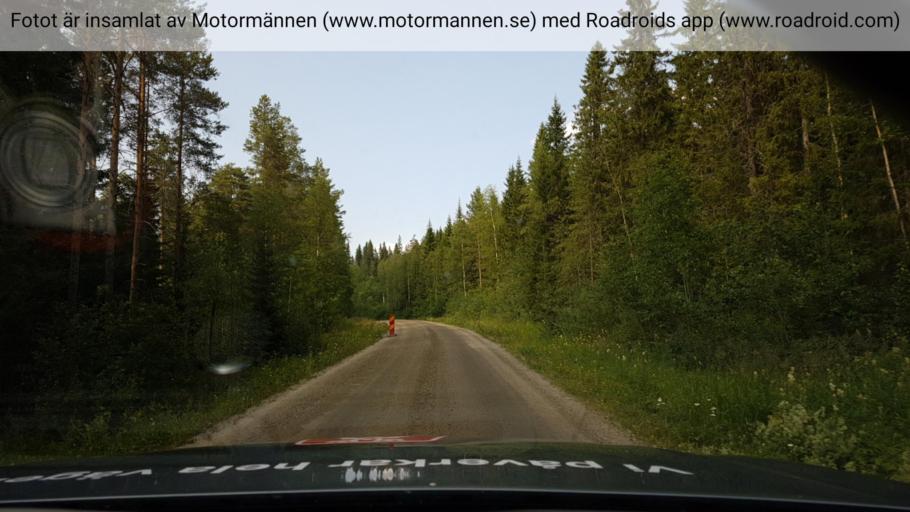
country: SE
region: Jaemtland
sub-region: OEstersunds Kommun
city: Brunflo
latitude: 62.5726
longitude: 14.9042
